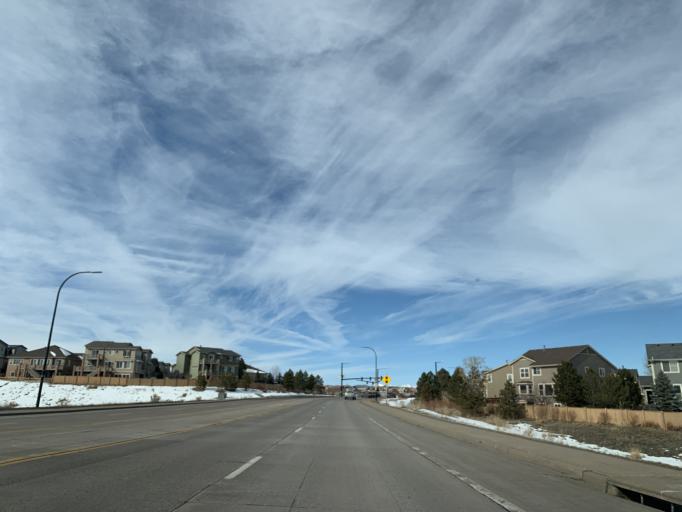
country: US
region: Colorado
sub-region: Douglas County
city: Carriage Club
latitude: 39.5217
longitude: -104.9285
